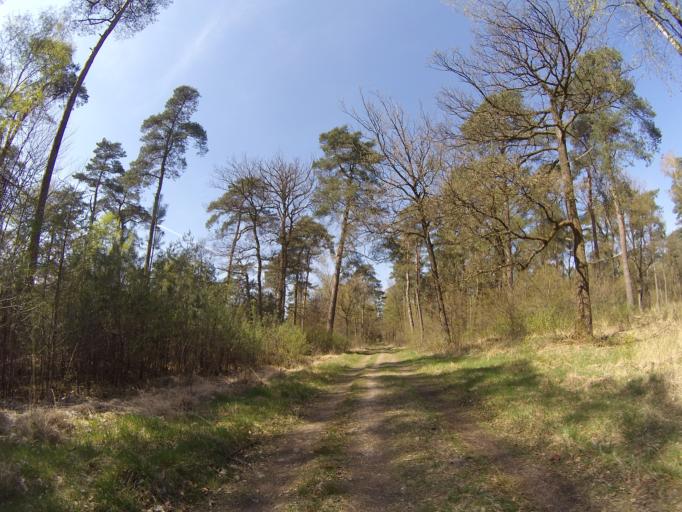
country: NL
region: Utrecht
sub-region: Gemeente Utrechtse Heuvelrug
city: Maarn
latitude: 52.0787
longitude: 5.3370
